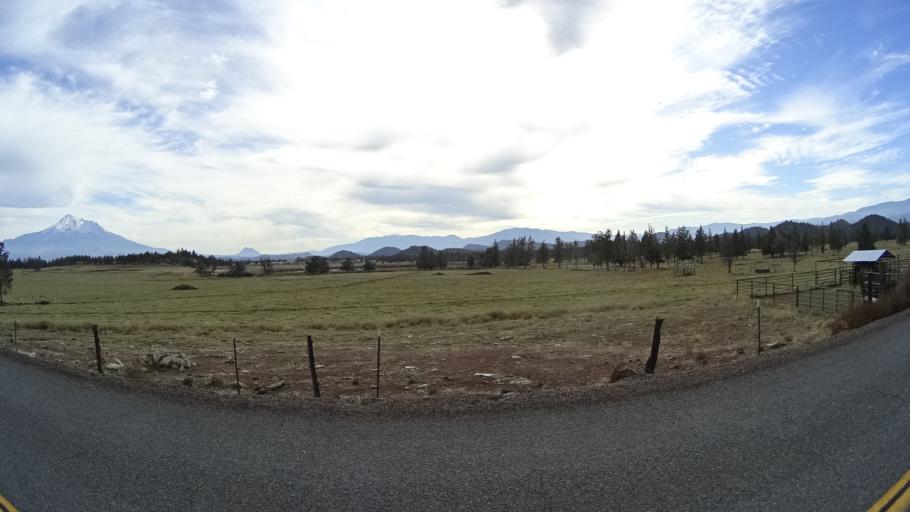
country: US
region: California
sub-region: Siskiyou County
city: Montague
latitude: 41.6377
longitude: -122.4324
